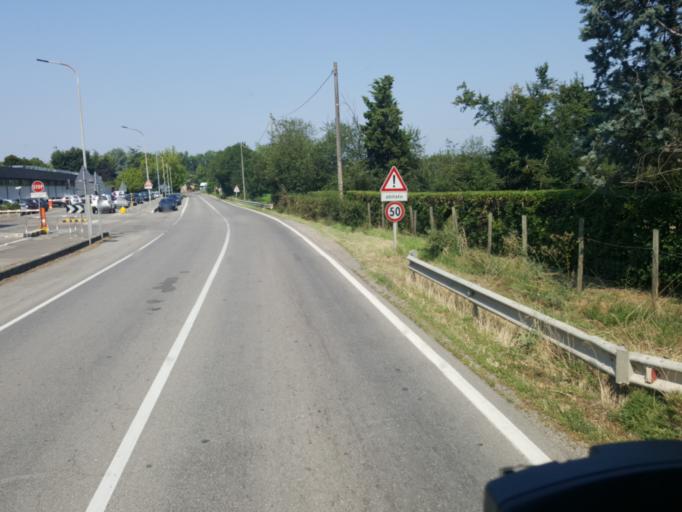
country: IT
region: Emilia-Romagna
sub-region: Provincia di Modena
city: Ca' di Sola
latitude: 44.5393
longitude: 10.9686
